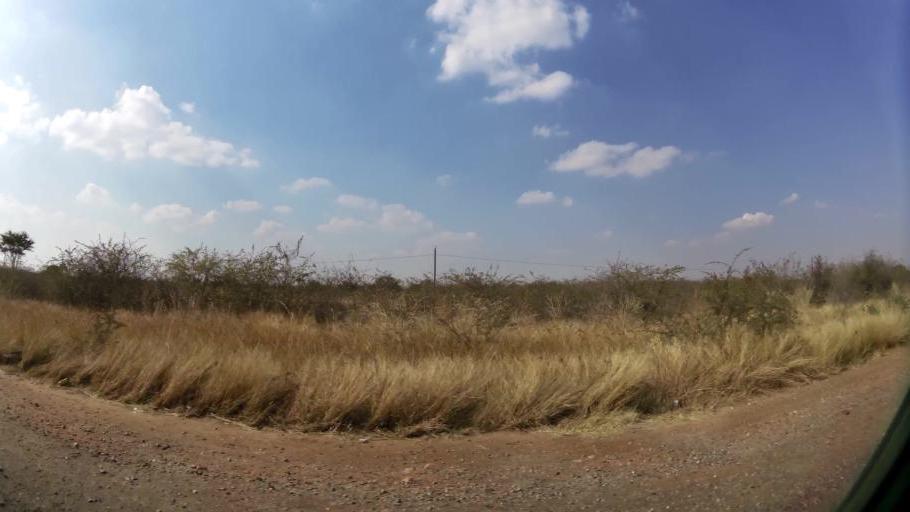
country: ZA
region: North-West
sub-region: Bojanala Platinum District Municipality
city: Rustenburg
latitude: -25.5124
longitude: 27.1003
